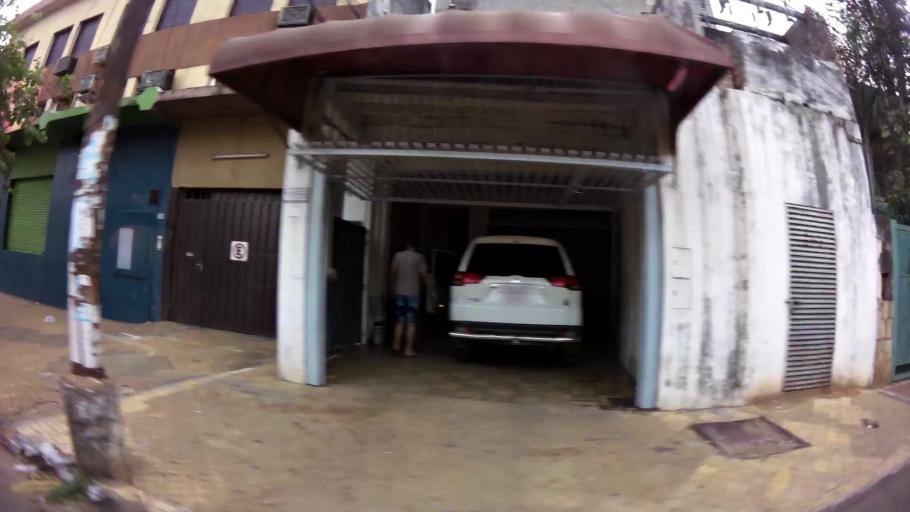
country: PY
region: Asuncion
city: Asuncion
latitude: -25.3025
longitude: -57.6139
